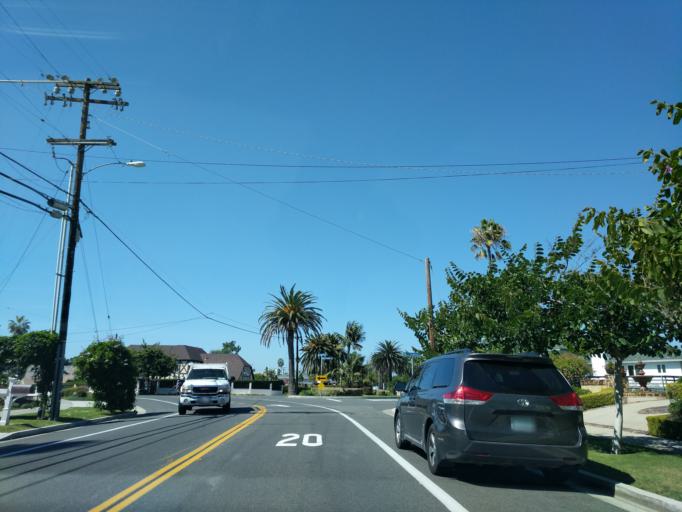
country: US
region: California
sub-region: Orange County
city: Dana Point
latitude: 33.4538
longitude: -117.6623
